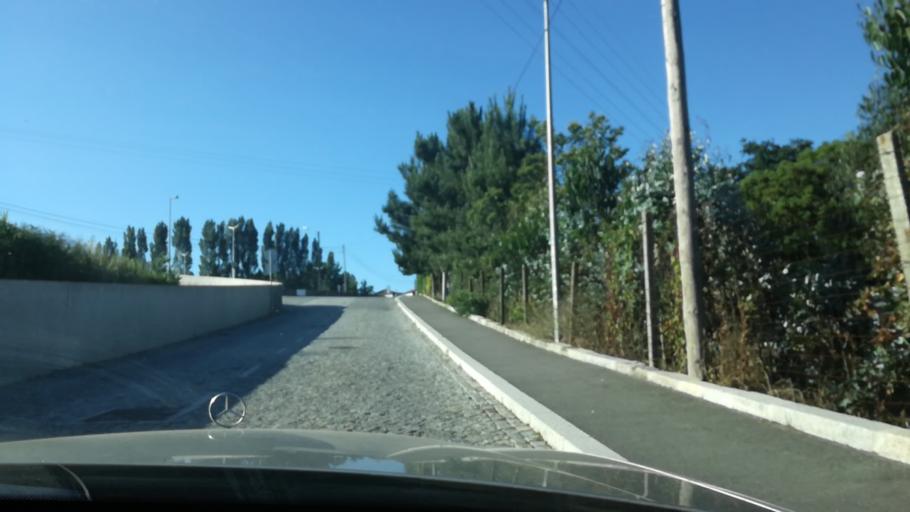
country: PT
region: Porto
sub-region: Maia
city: Leca do Bailio
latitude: 41.2186
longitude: -8.6239
